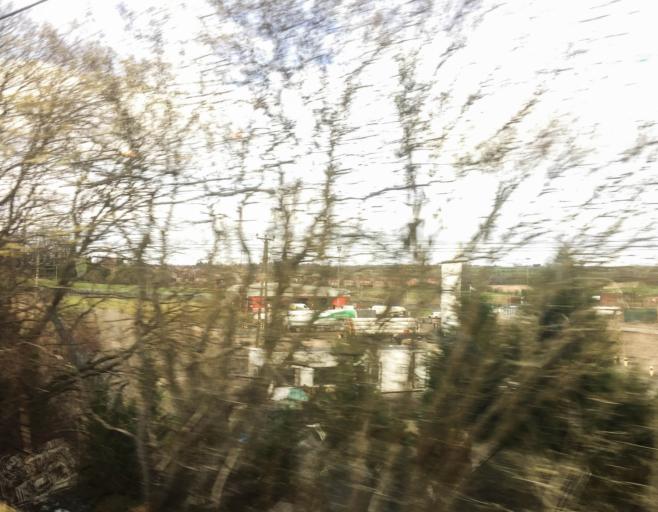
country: GB
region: Scotland
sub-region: North Lanarkshire
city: Newarthill
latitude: 55.8016
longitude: -3.9548
